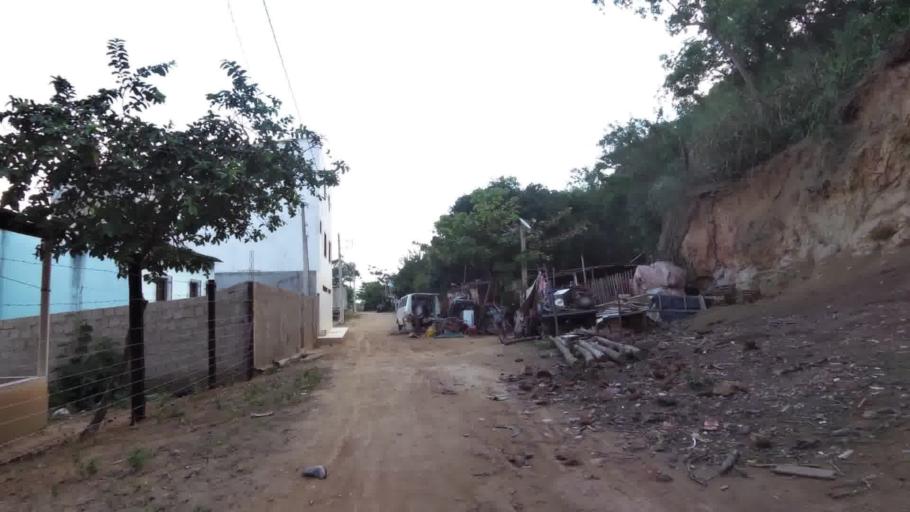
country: BR
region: Espirito Santo
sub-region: Piuma
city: Piuma
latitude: -20.8407
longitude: -40.7494
